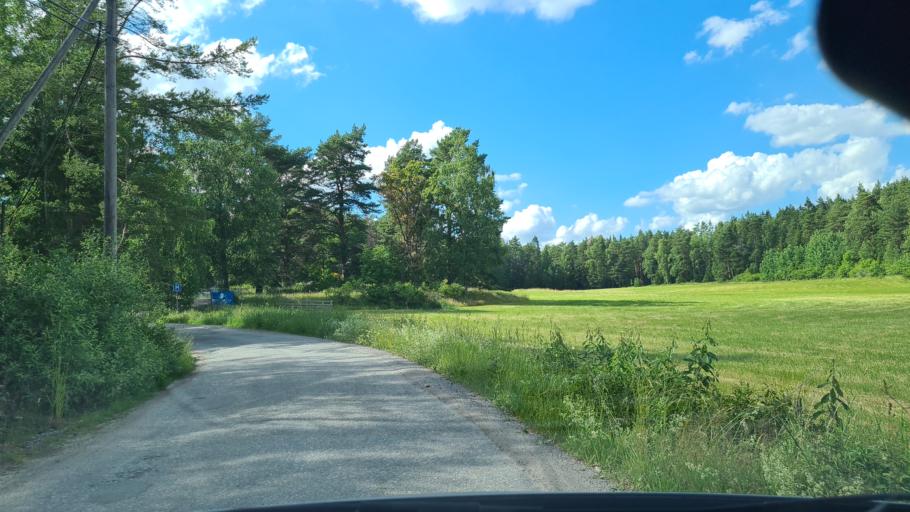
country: SE
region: Stockholm
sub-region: Vaxholms Kommun
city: Vaxholm
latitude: 59.4097
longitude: 18.3889
